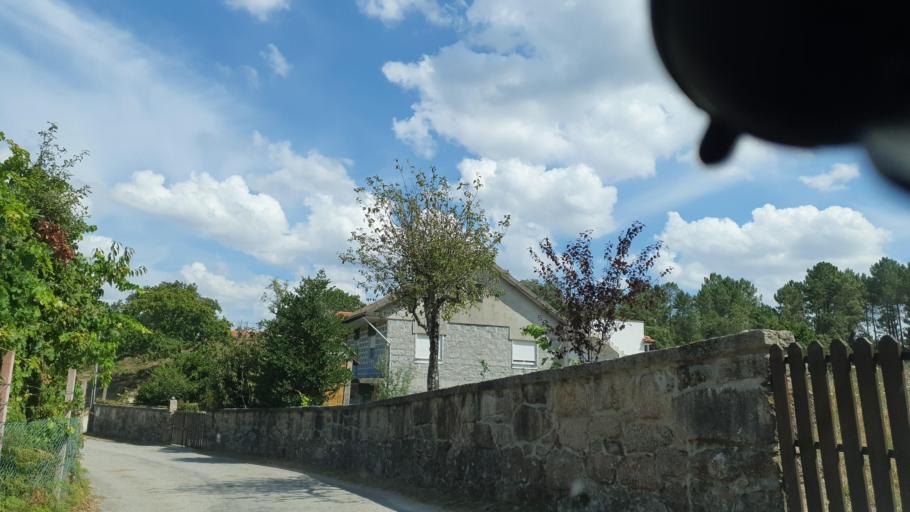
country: PT
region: Braga
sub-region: Vieira do Minho
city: Vieira do Minho
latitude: 41.7056
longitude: -8.0512
